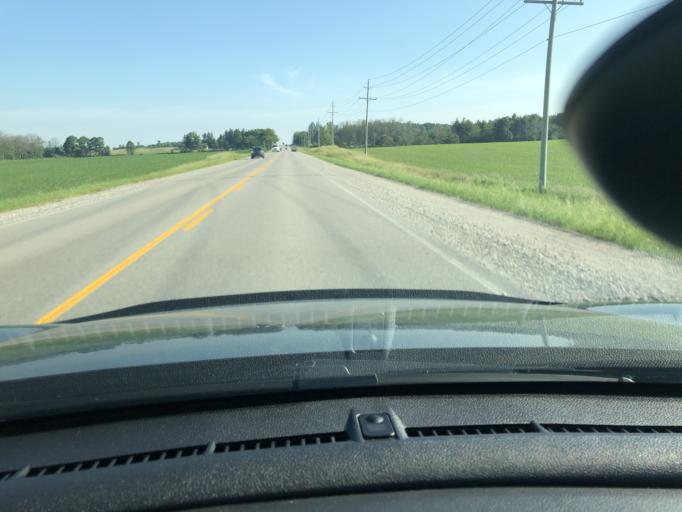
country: CA
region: Ontario
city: Stratford
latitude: 43.3920
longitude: -80.8373
